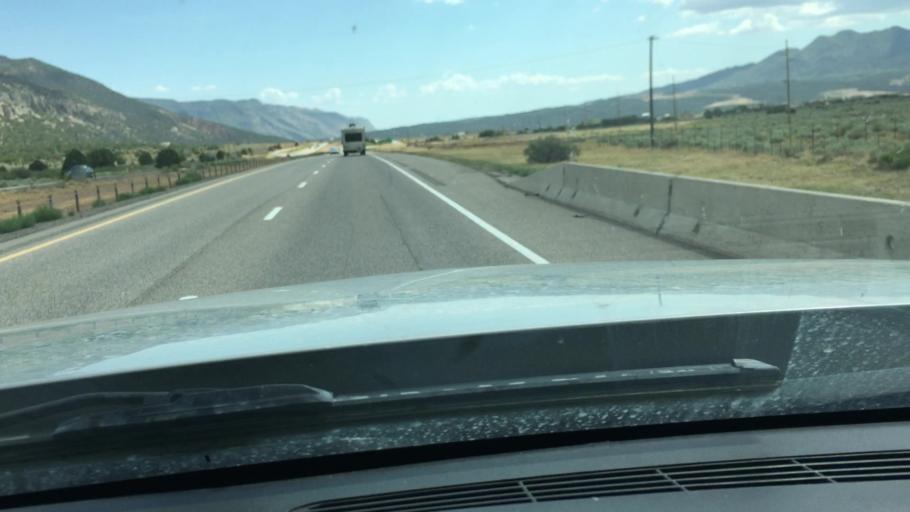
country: US
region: Utah
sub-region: Washington County
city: Toquerville
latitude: 37.4623
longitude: -113.2263
